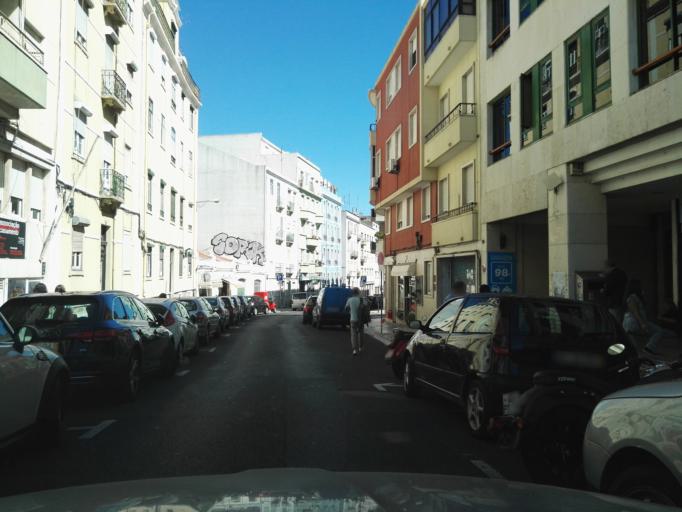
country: PT
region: Lisbon
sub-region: Lisbon
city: Lisbon
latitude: 38.7307
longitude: -9.1400
